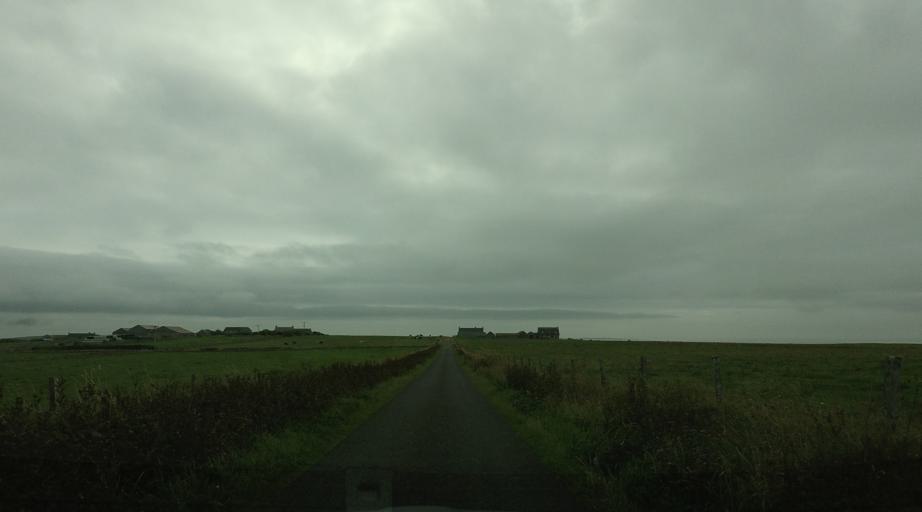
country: GB
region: Scotland
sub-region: Orkney Islands
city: Orkney
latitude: 58.7654
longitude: -2.9627
